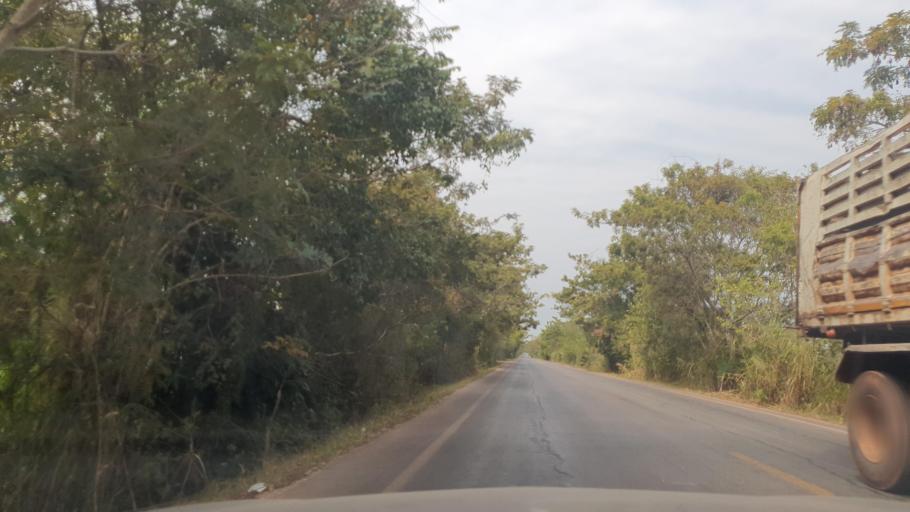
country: TH
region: Changwat Bueng Kan
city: Bung Khla
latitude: 18.2175
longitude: 104.0401
